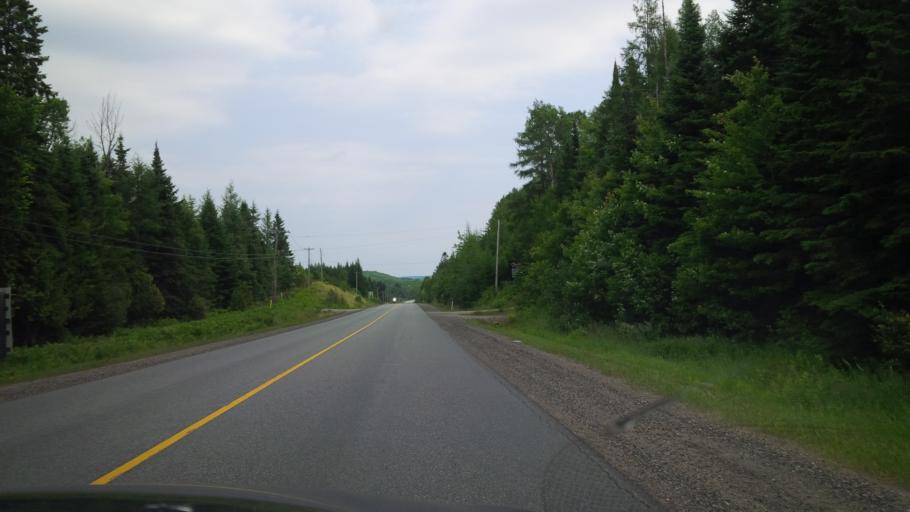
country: CA
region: Ontario
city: Huntsville
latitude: 45.5382
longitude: -79.2840
